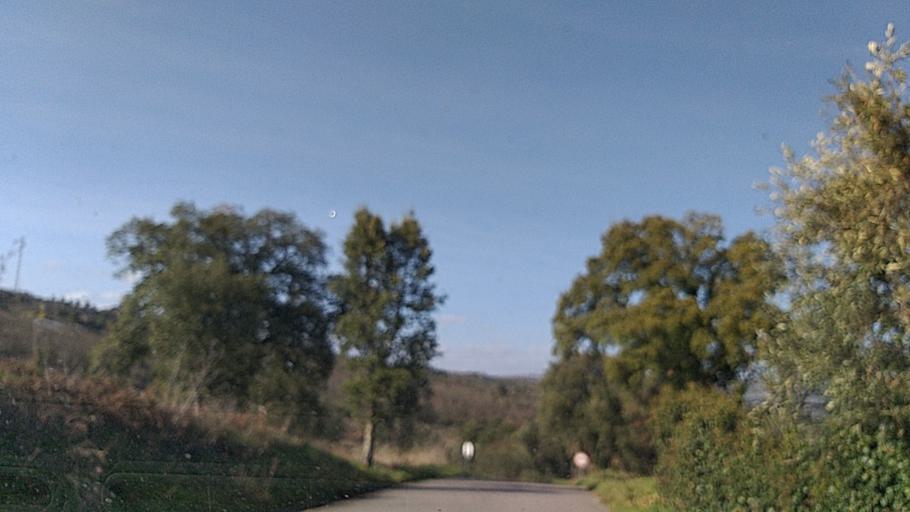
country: PT
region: Guarda
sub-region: Celorico da Beira
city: Celorico da Beira
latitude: 40.6363
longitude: -7.3972
